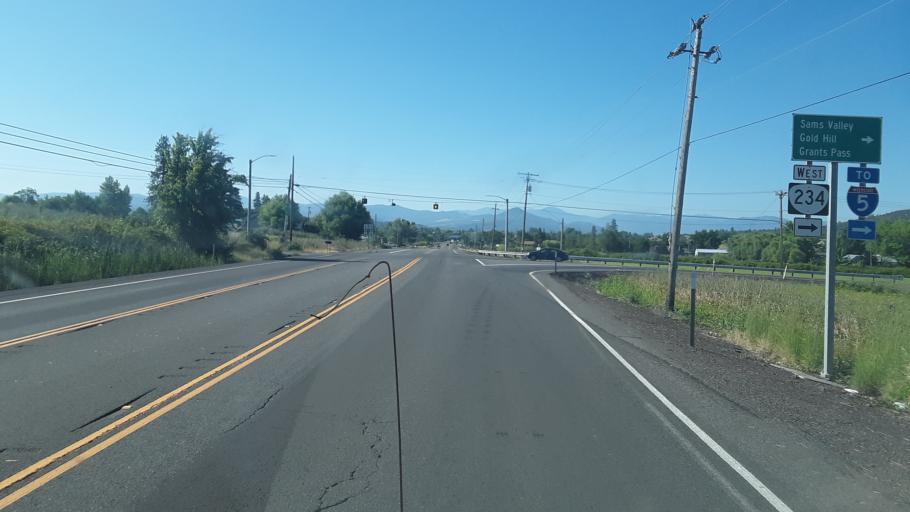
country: US
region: Oregon
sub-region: Jackson County
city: Eagle Point
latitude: 42.5245
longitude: -122.8143
